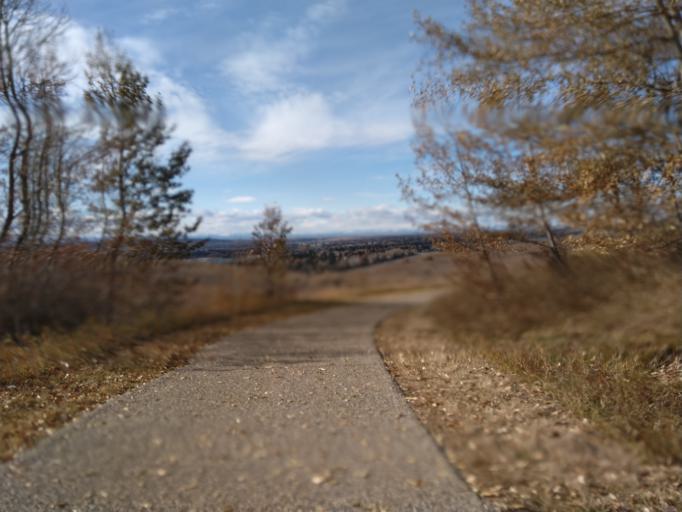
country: CA
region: Alberta
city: Calgary
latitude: 51.1035
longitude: -114.1131
